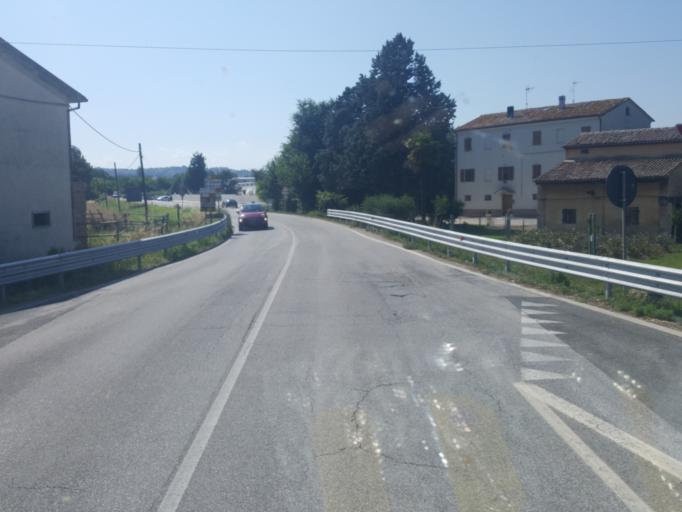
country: IT
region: The Marches
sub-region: Provincia di Ancona
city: Borghetto
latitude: 43.5543
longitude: 13.2988
